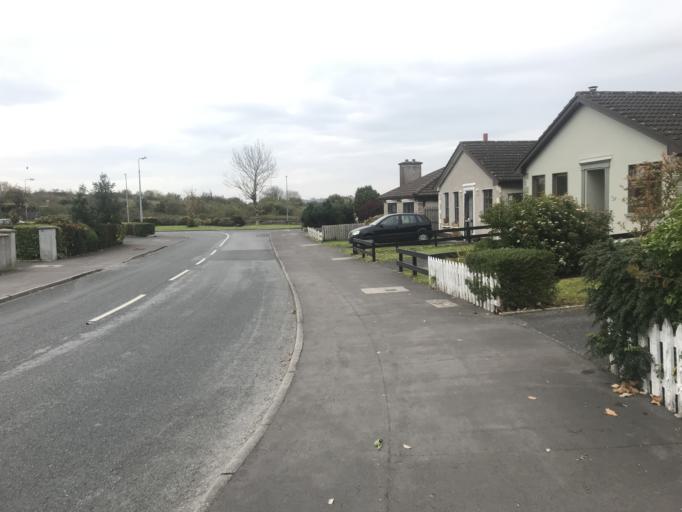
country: IE
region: Connaught
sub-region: County Galway
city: Gaillimh
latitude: 53.2926
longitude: -9.0507
